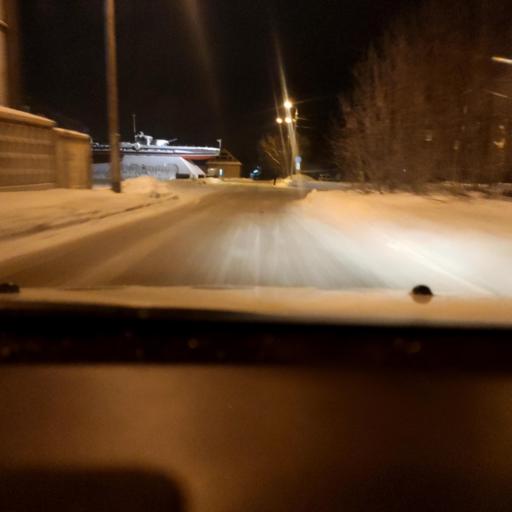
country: RU
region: Perm
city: Kondratovo
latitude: 58.0348
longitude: 56.0377
